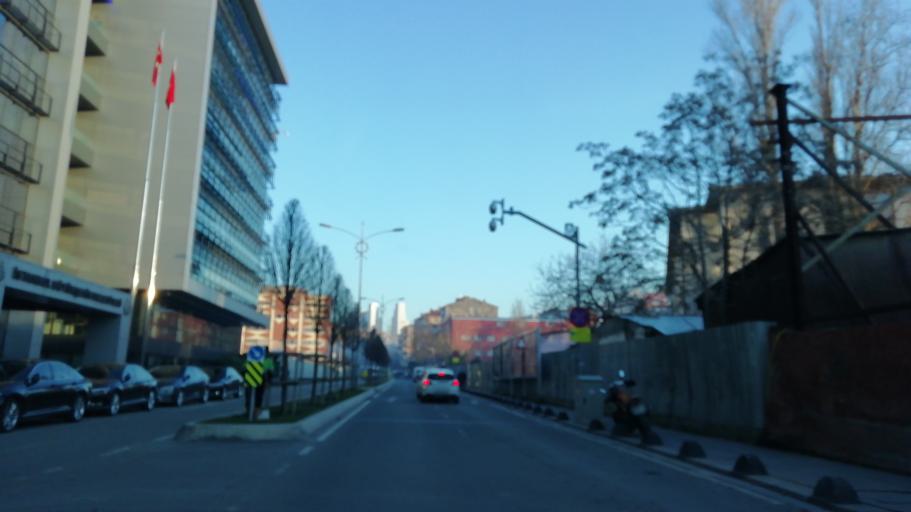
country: TR
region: Istanbul
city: Eminoenue
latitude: 41.0391
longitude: 28.9717
